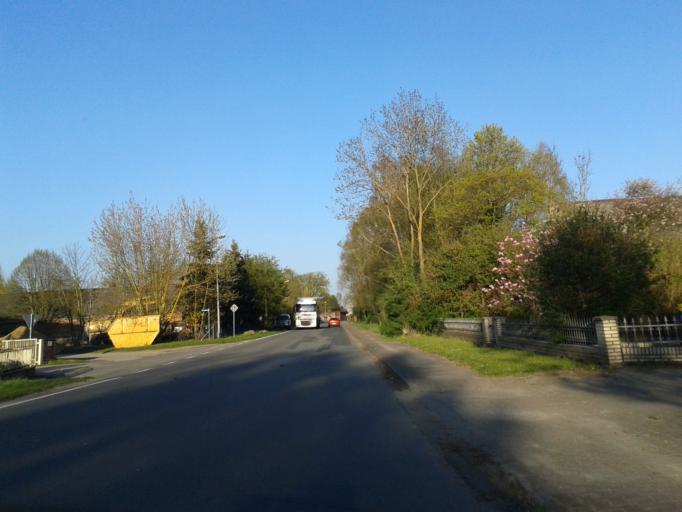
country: DE
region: Lower Saxony
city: Wustrow
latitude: 52.9394
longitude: 11.0944
